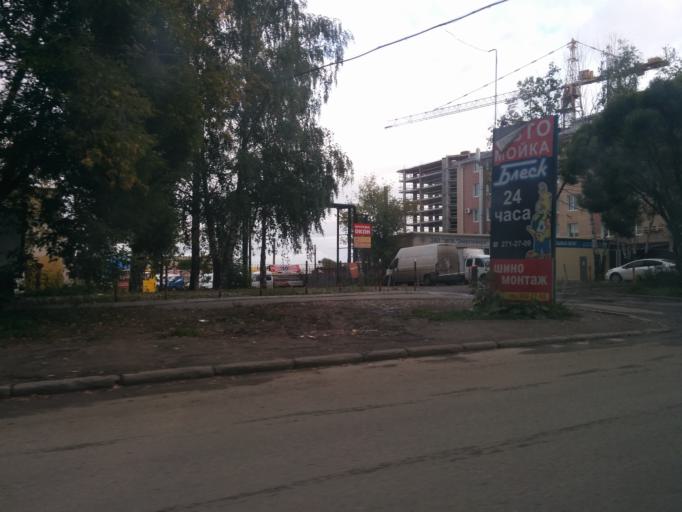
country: RU
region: Perm
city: Perm
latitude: 57.9969
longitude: 56.3033
